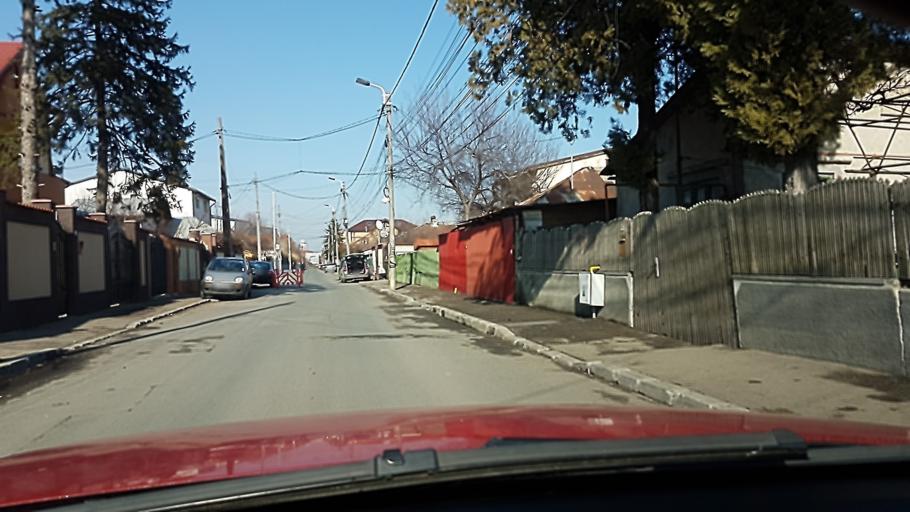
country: RO
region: Ilfov
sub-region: Comuna Pantelimon
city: Pantelimon
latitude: 44.4283
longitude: 26.1966
